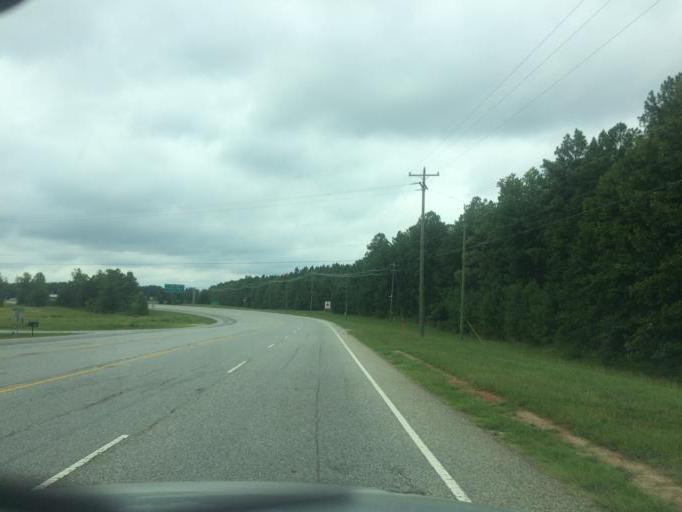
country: US
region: South Carolina
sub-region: Greenville County
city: Greer
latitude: 34.8947
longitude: -82.1973
